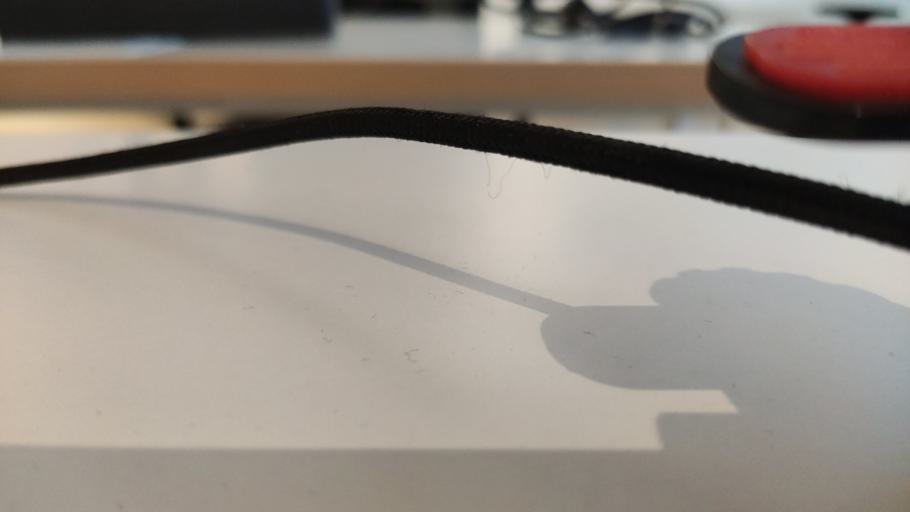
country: RU
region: Moskovskaya
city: Novopetrovskoye
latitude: 55.8743
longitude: 36.4045
